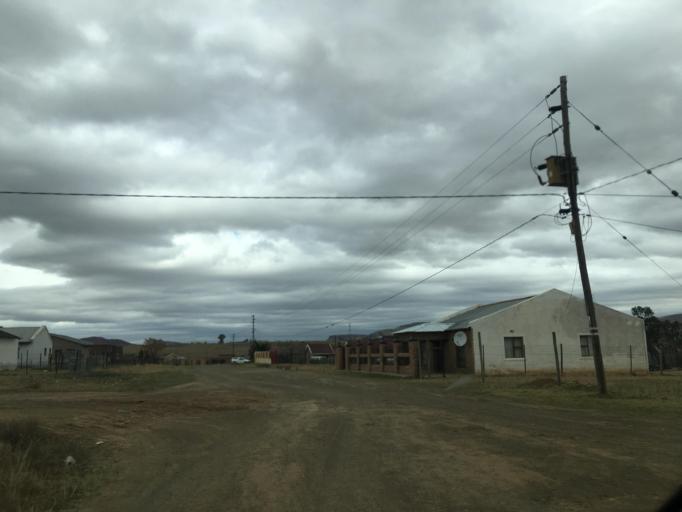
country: ZA
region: Eastern Cape
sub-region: Chris Hani District Municipality
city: Cala
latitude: -31.5363
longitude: 27.6909
